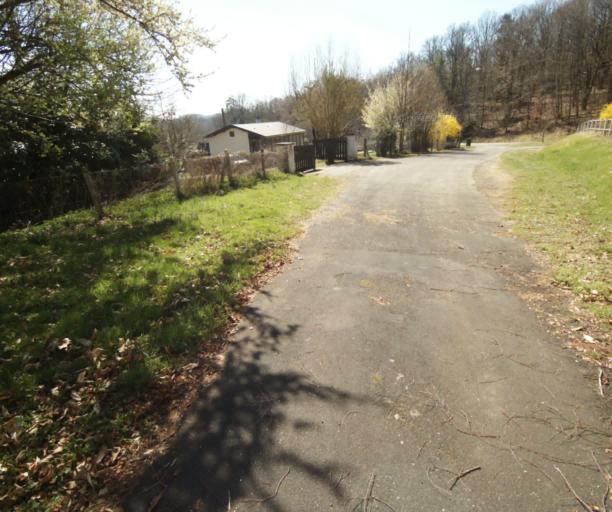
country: FR
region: Limousin
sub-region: Departement de la Correze
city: Saint-Clement
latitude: 45.3457
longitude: 1.6402
